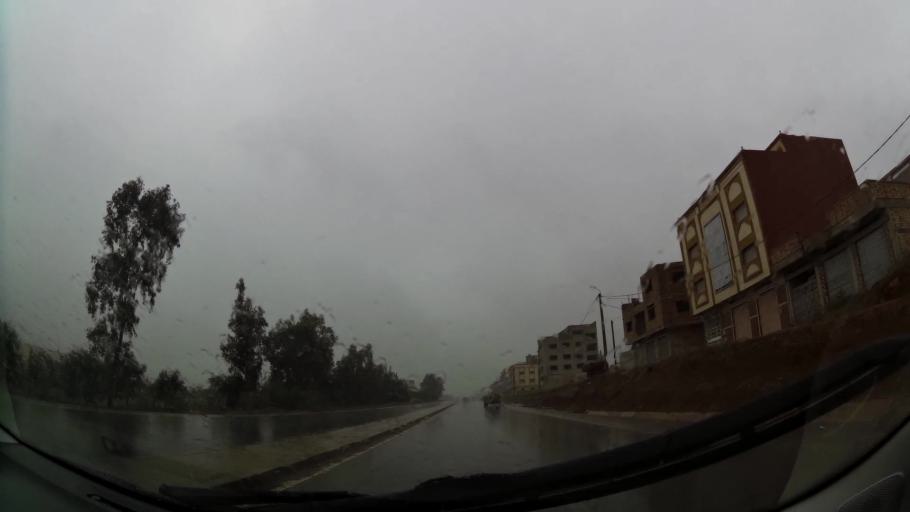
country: MA
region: Taza-Al Hoceima-Taounate
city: Imzourene
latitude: 35.1230
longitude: -3.8446
